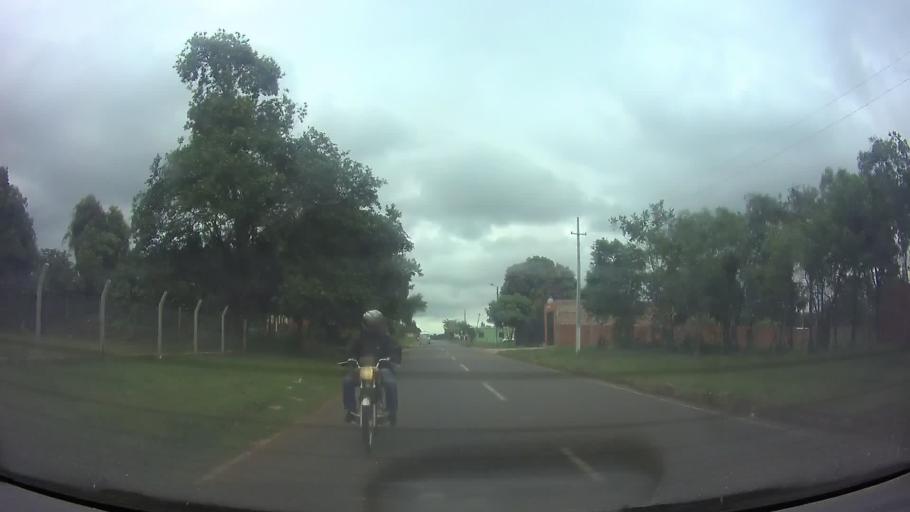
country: PY
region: Paraguari
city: Carapegua
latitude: -25.7613
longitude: -57.2515
